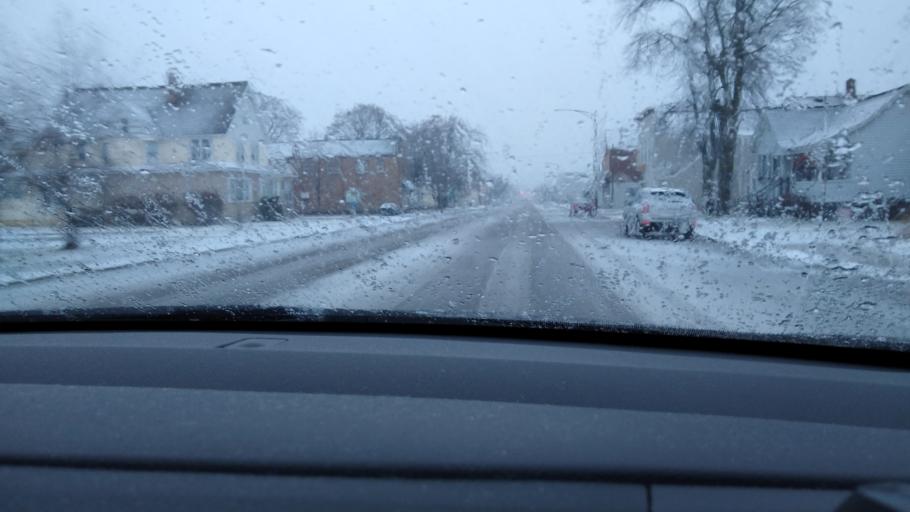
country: US
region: Michigan
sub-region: Delta County
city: Escanaba
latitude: 45.7415
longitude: -87.0612
